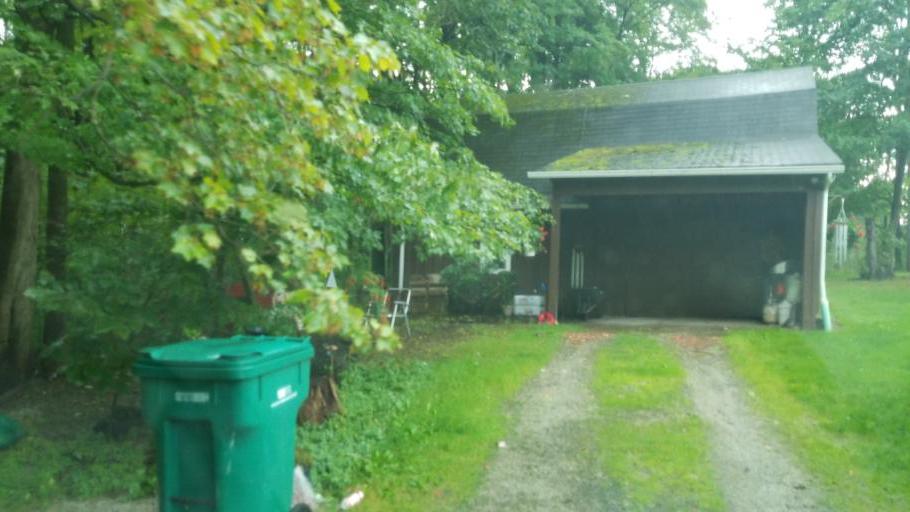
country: US
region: Ohio
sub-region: Geauga County
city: Middlefield
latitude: 41.4704
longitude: -80.9704
